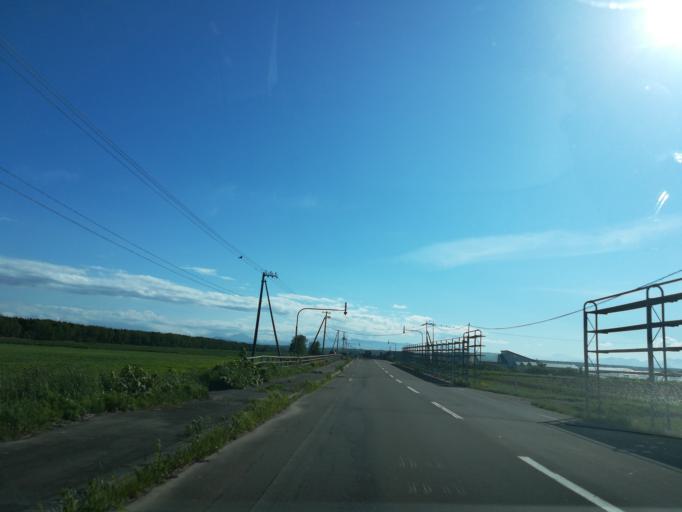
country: JP
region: Hokkaido
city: Ebetsu
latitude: 43.0470
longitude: 141.5968
